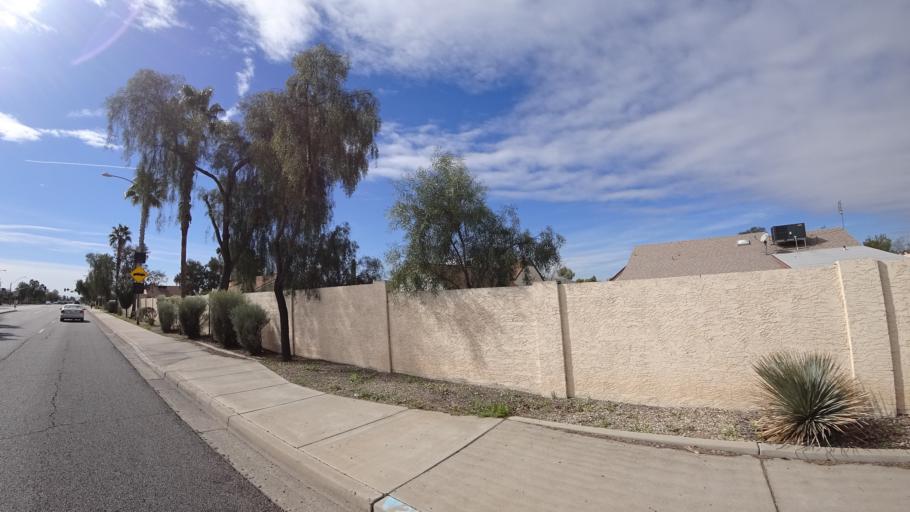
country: US
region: Arizona
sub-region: Maricopa County
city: Peoria
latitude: 33.6156
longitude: -112.1859
